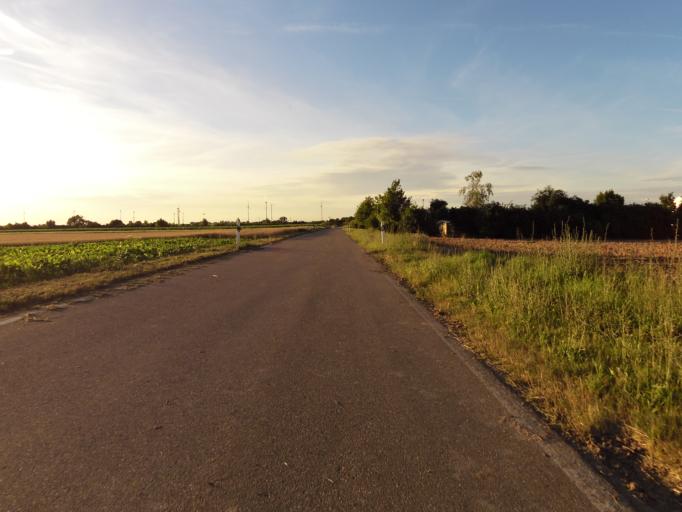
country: DE
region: Rheinland-Pfalz
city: Hessheim
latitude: 49.5551
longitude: 8.3056
